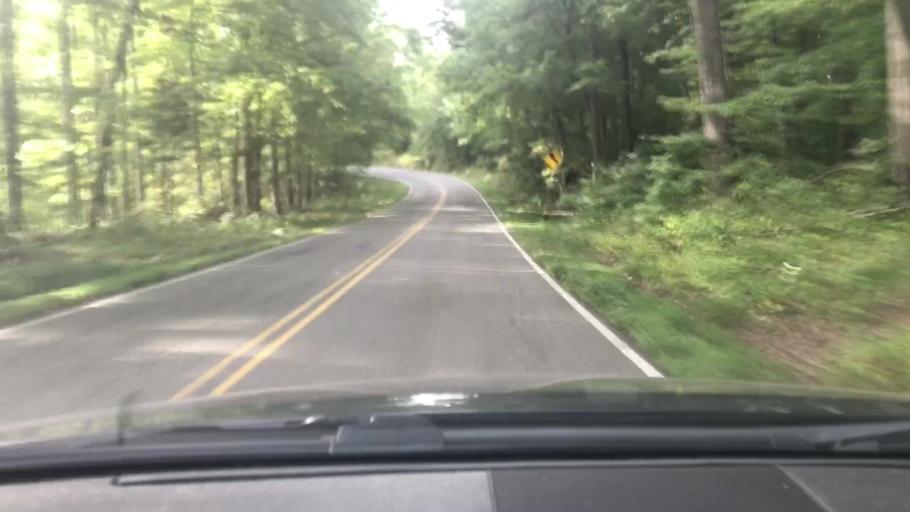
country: US
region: Tennessee
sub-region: Dickson County
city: White Bluff
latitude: 36.1568
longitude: -87.2504
